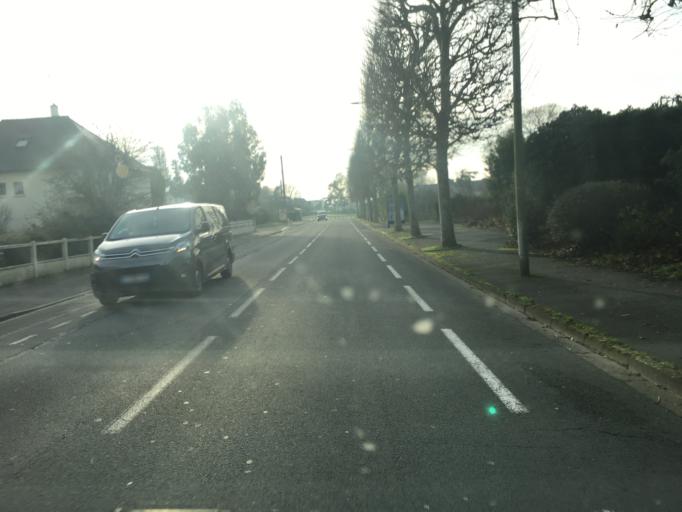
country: FR
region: Lower Normandy
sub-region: Departement du Calvados
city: Cabourg
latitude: 49.2844
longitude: -0.1169
